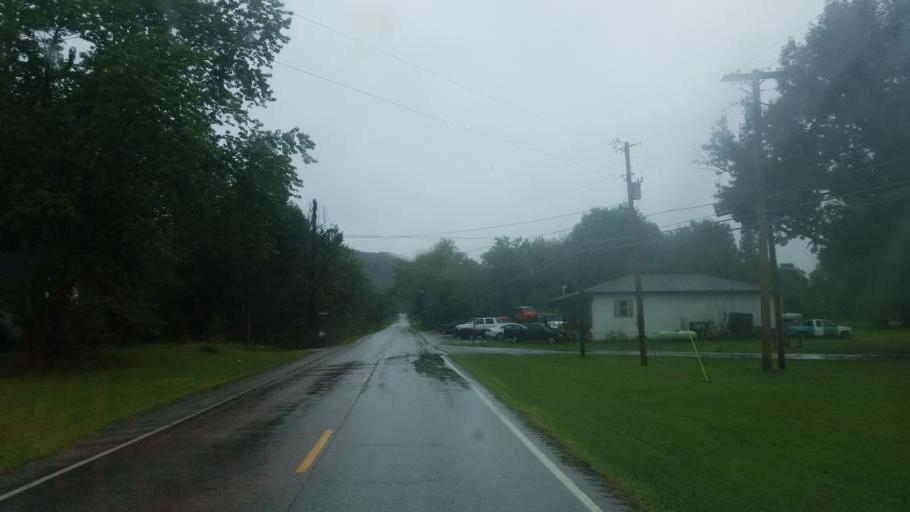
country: US
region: Kentucky
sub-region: Greenup County
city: South Shore
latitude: 38.6874
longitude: -82.9257
